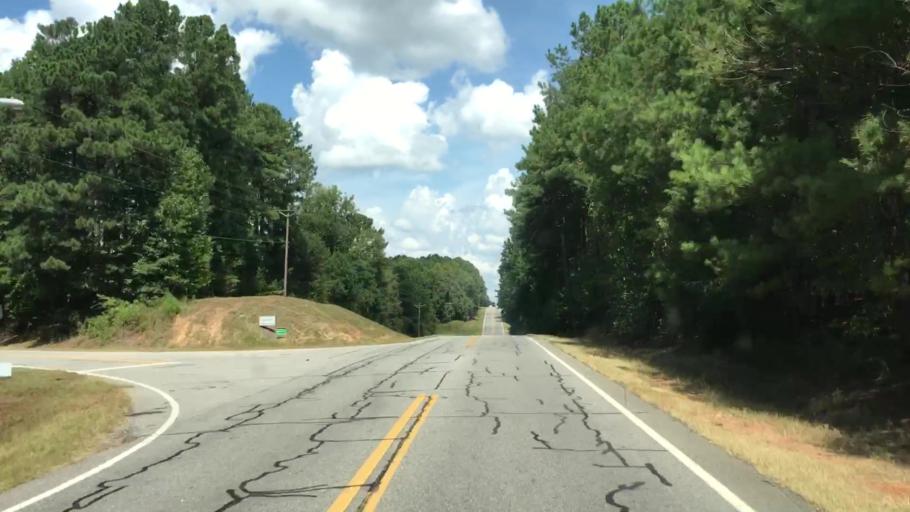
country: US
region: Georgia
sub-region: Oconee County
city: Watkinsville
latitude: 33.7653
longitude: -83.3094
